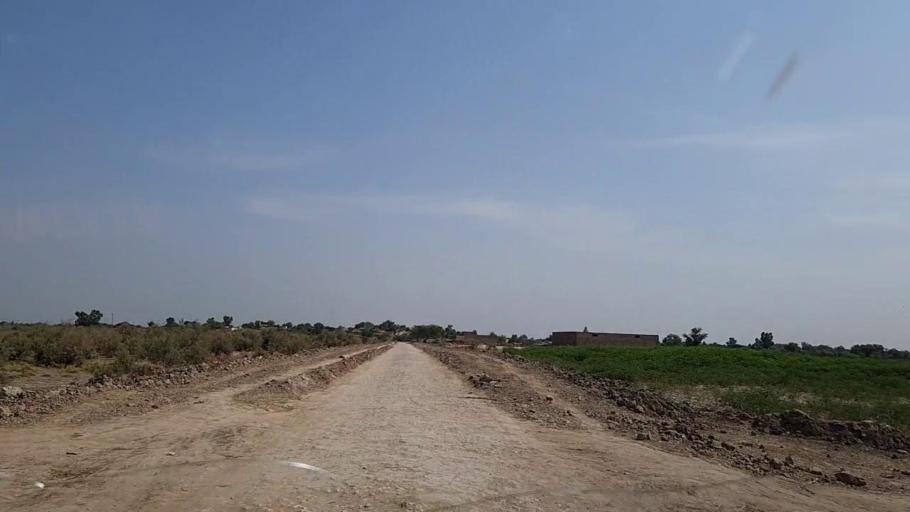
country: PK
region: Sindh
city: Khanpur
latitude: 27.7538
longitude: 69.3369
